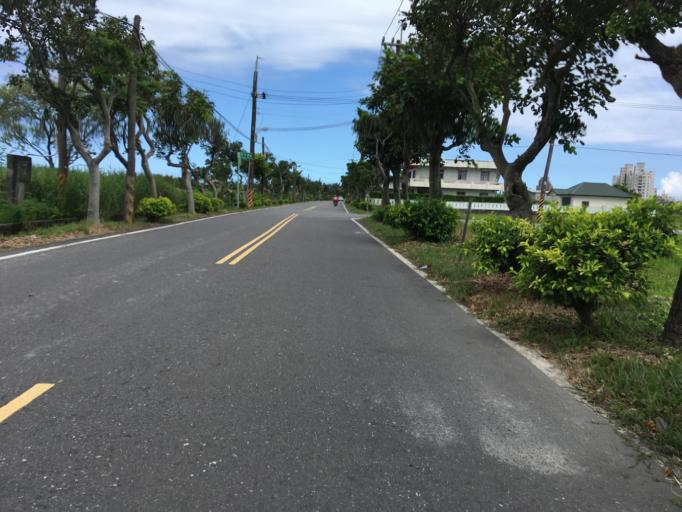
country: TW
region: Taiwan
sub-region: Yilan
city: Yilan
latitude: 24.6843
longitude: 121.8050
